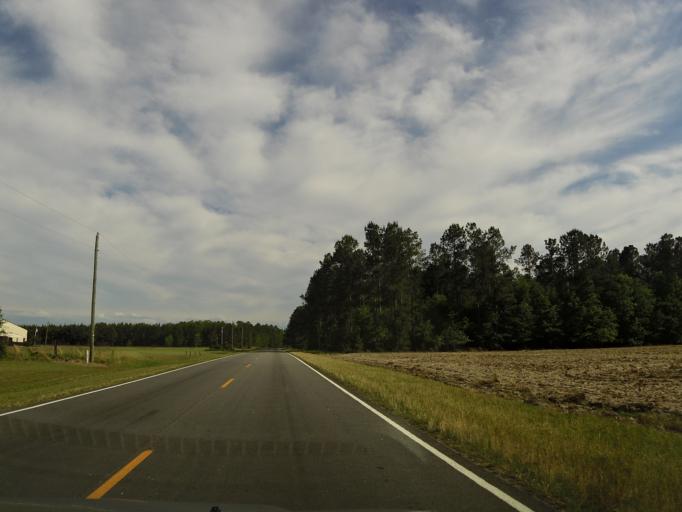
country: US
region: South Carolina
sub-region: Allendale County
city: Fairfax
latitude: 33.0201
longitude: -81.2175
